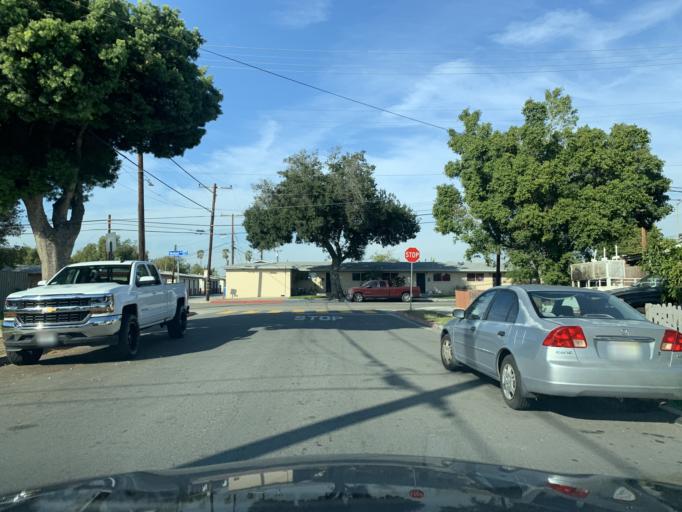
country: US
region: California
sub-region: Orange County
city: Anaheim
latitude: 33.8236
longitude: -117.9065
